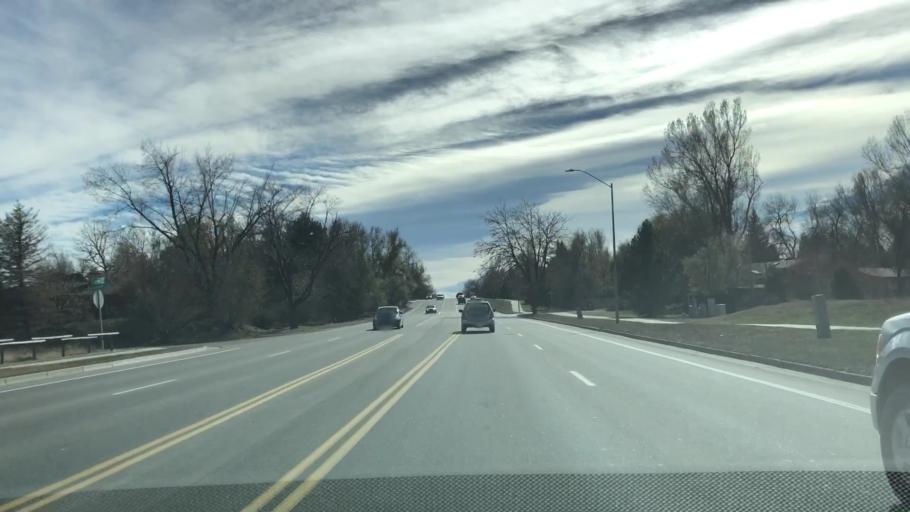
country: US
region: Colorado
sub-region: Larimer County
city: Fort Collins
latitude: 40.5657
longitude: -105.1152
